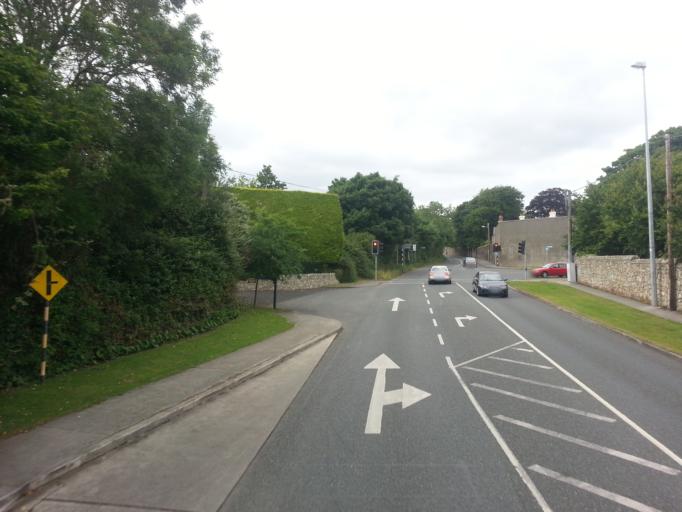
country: IE
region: Leinster
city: Sandyford
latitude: 53.2622
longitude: -6.2115
